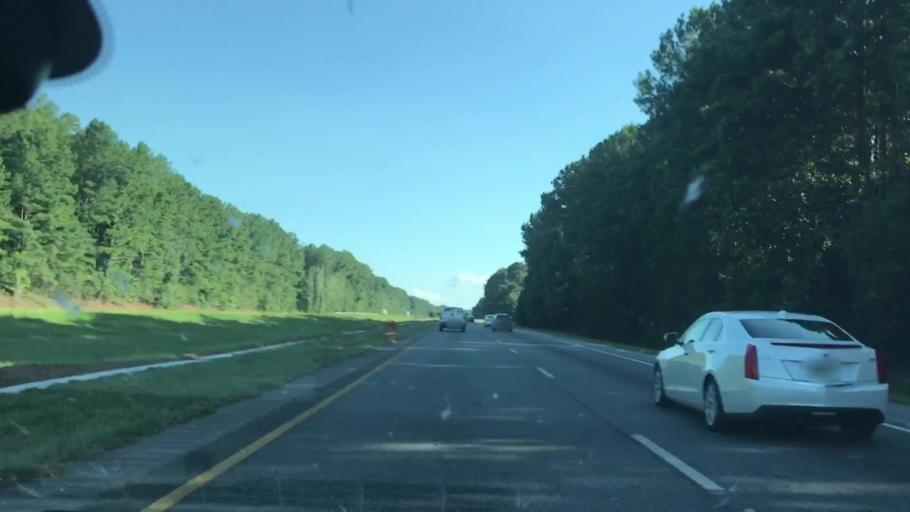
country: US
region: Georgia
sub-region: Harris County
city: Hamilton
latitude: 32.7932
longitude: -85.0212
